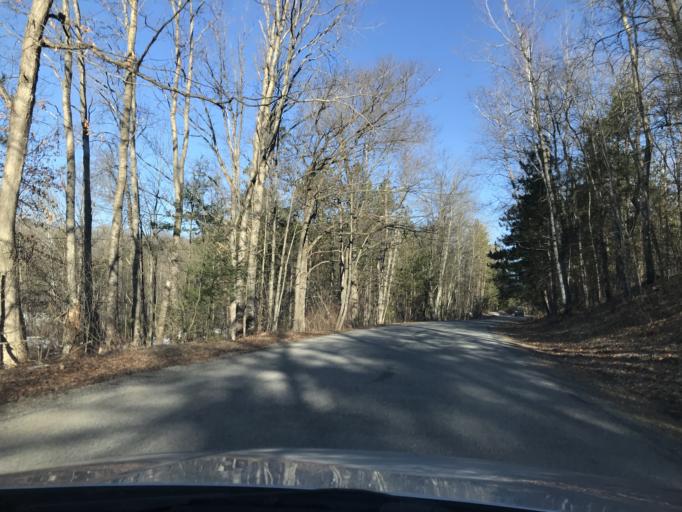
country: US
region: Wisconsin
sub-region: Marinette County
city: Niagara
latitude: 45.3906
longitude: -88.0517
